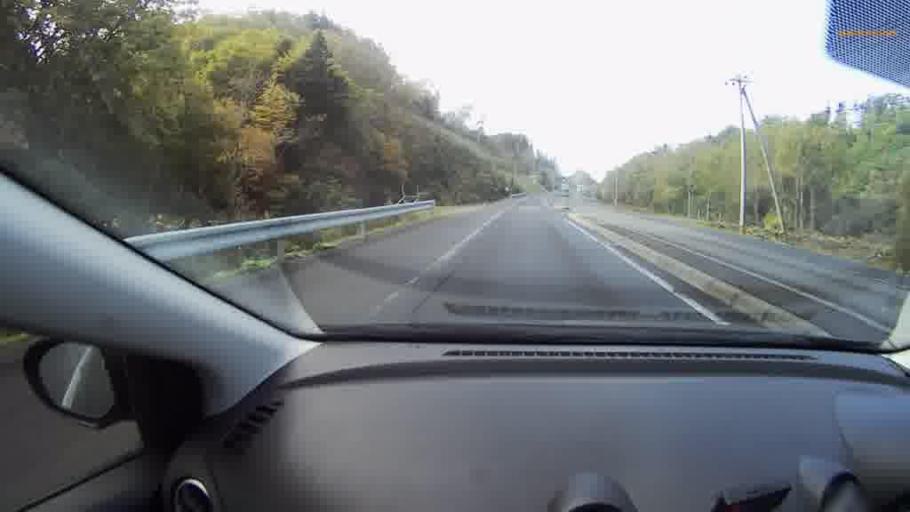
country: JP
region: Hokkaido
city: Kushiro
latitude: 43.0075
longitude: 144.5091
